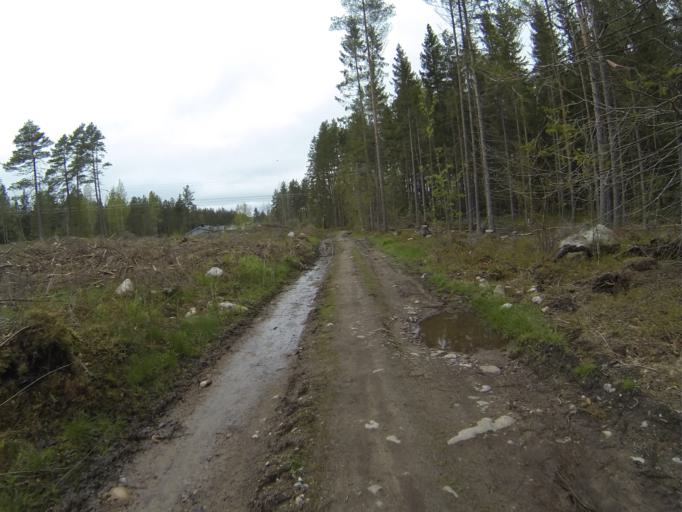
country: FI
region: Varsinais-Suomi
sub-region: Salo
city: Salo
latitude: 60.4037
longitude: 23.1991
